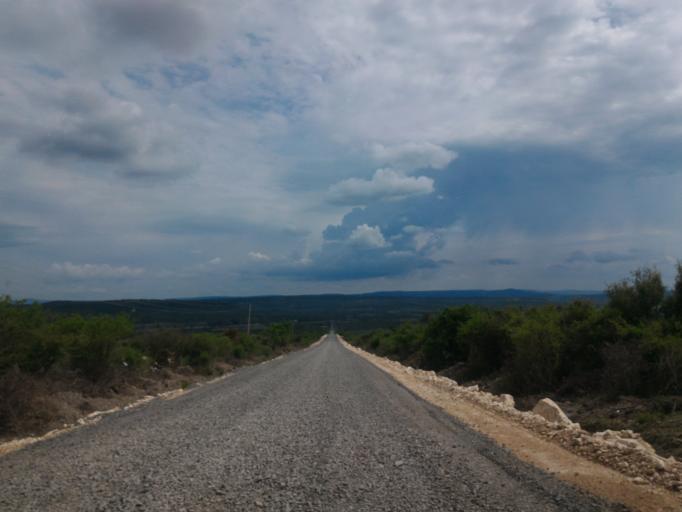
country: MX
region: Jalisco
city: San Diego de Alejandria
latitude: 20.9145
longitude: -102.0439
